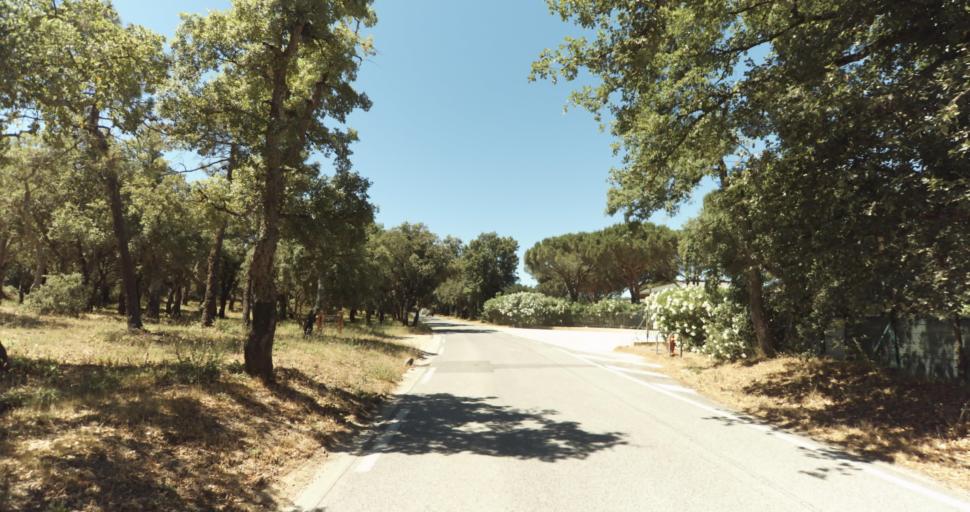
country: FR
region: Provence-Alpes-Cote d'Azur
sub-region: Departement du Var
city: Gassin
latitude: 43.2521
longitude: 6.5831
